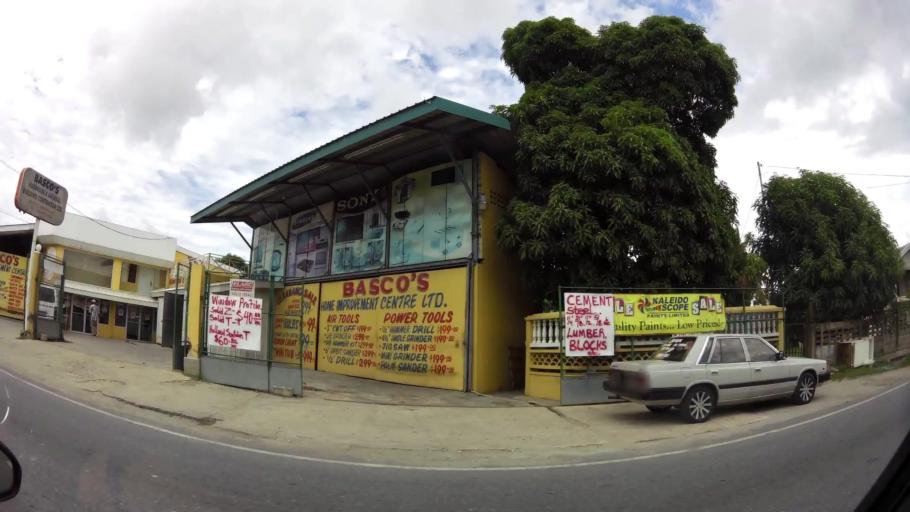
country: TT
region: Couva-Tabaquite-Talparo
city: Couva
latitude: 10.4482
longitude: -61.4441
